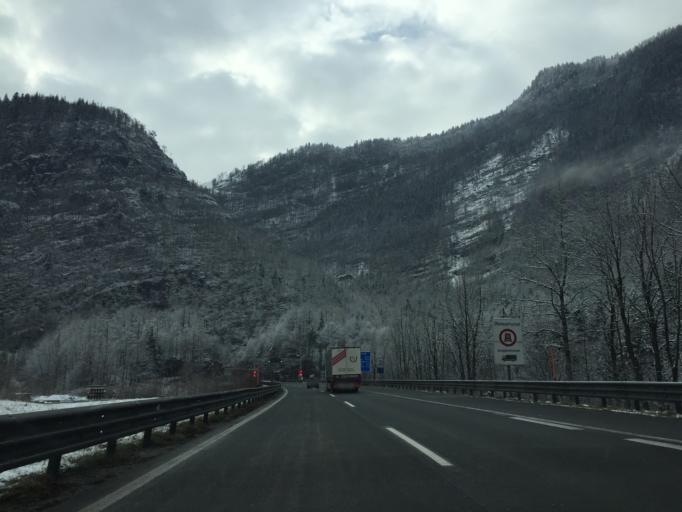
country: AT
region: Salzburg
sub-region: Politischer Bezirk Hallein
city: Golling an der Salzach
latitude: 47.5799
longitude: 13.1597
